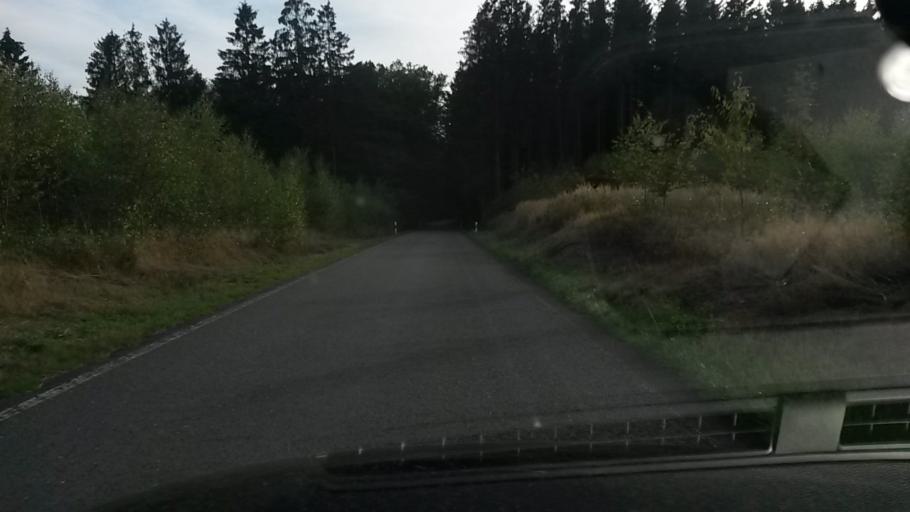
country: DE
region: North Rhine-Westphalia
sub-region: Regierungsbezirk Arnsberg
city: Herscheid
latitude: 51.1951
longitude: 7.7523
